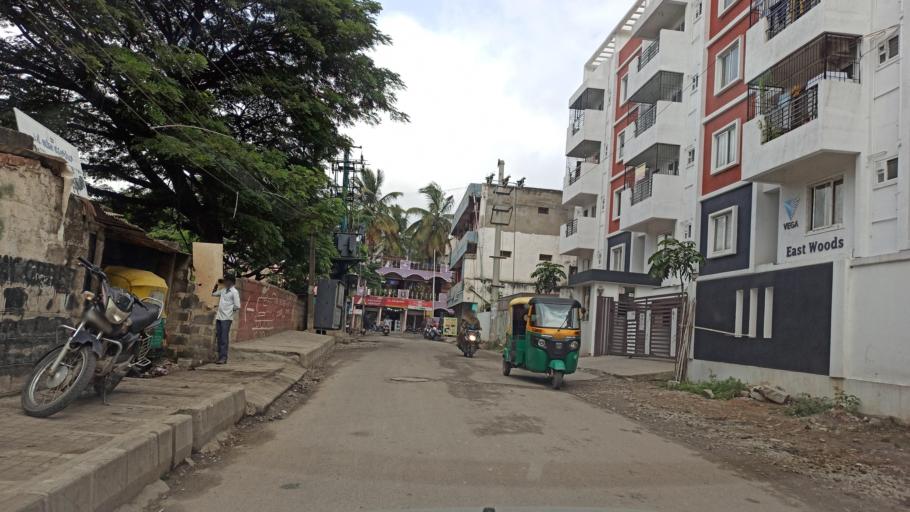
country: IN
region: Karnataka
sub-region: Bangalore Urban
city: Bangalore
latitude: 13.0018
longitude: 77.6754
